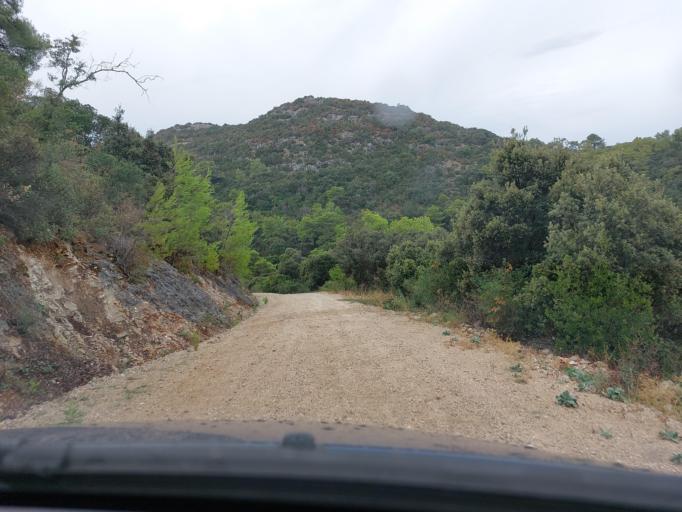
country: HR
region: Dubrovacko-Neretvanska
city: Smokvica
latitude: 42.7488
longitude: 16.9142
